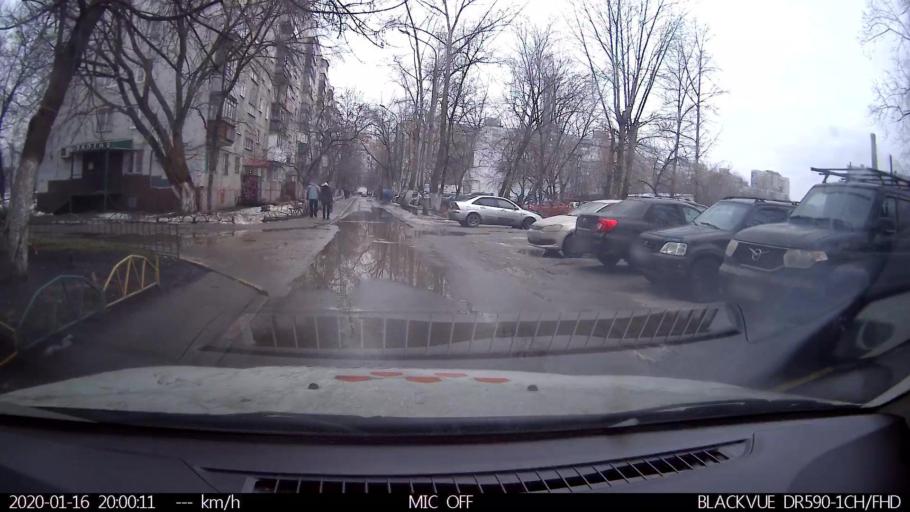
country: RU
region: Nizjnij Novgorod
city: Nizhniy Novgorod
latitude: 56.3205
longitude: 43.9374
